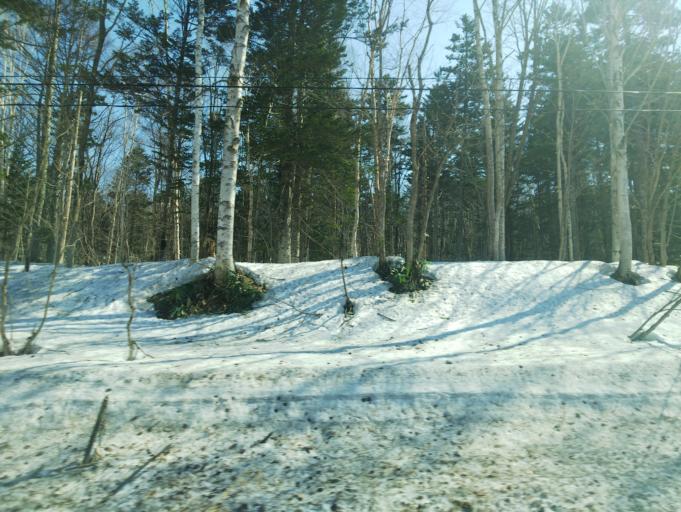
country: JP
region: Hokkaido
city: Nayoro
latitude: 44.7166
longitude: 142.2721
